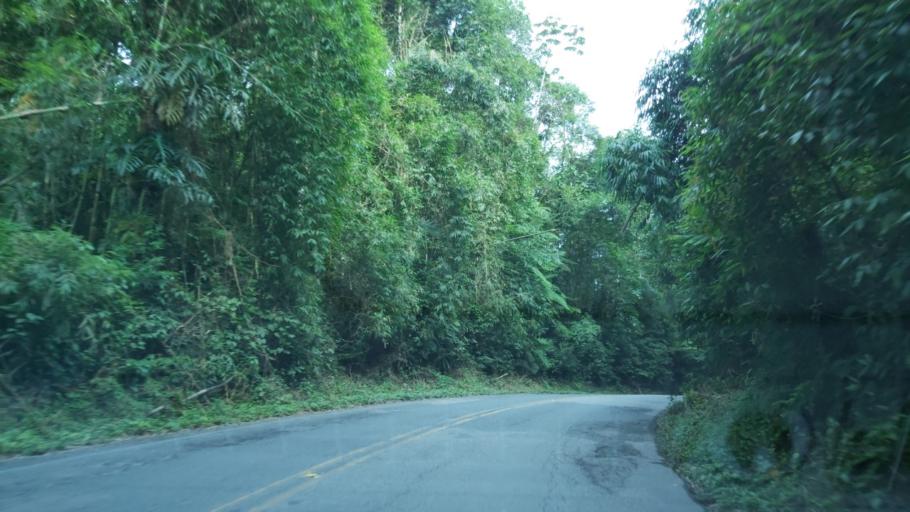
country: BR
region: Sao Paulo
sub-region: Juquia
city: Juquia
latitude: -24.0715
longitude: -47.6032
